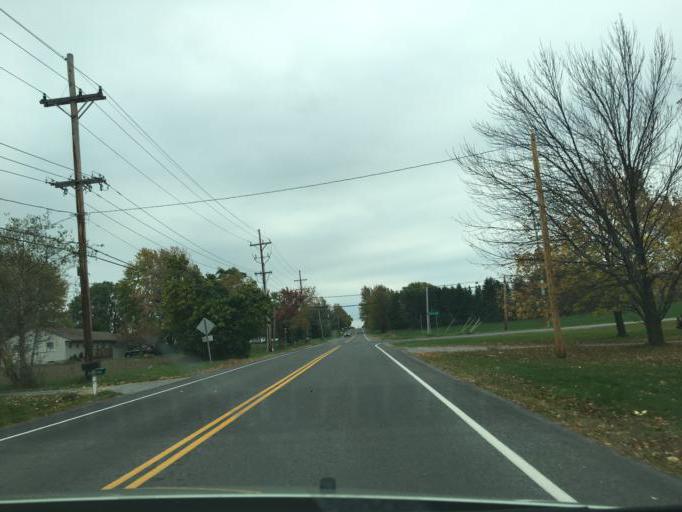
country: US
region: New York
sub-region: Ontario County
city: Canandaigua
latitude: 42.9321
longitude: -77.3121
